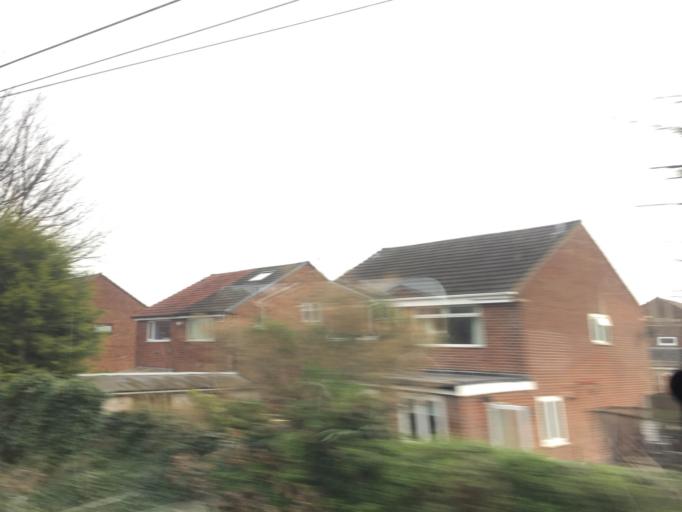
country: GB
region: England
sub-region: Lancashire
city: Euxton
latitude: 53.6619
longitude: -2.6719
